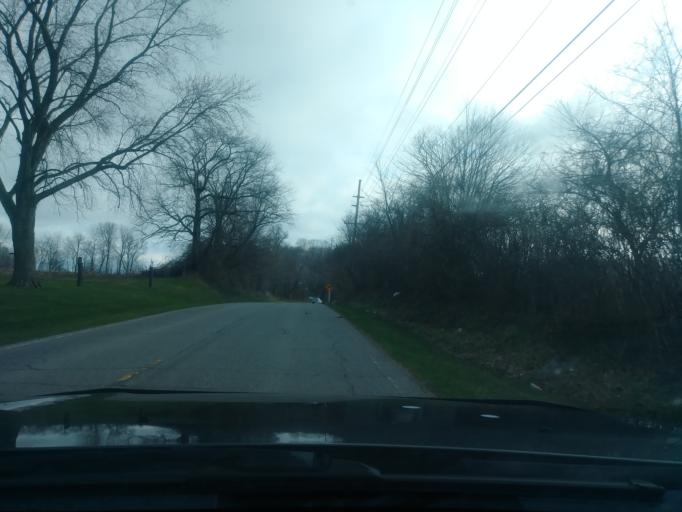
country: US
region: Indiana
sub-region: LaPorte County
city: LaPorte
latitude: 41.6171
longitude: -86.7964
